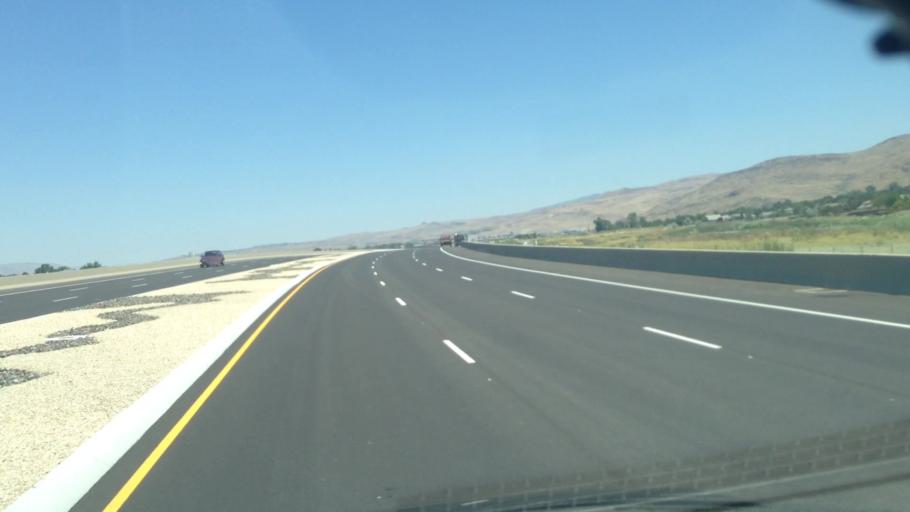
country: US
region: Nevada
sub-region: Washoe County
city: Sparks
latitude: 39.4863
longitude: -119.7359
